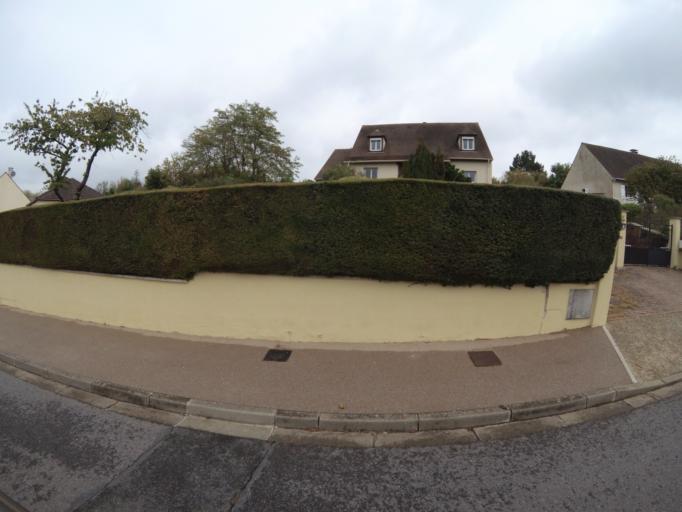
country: FR
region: Ile-de-France
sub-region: Departement de Seine-et-Marne
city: Gouvernes
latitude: 48.8479
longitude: 2.6897
